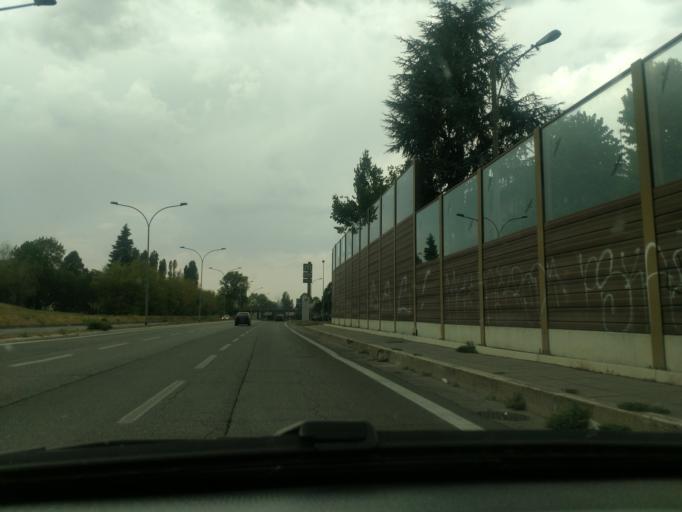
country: IT
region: Emilia-Romagna
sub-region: Provincia di Bologna
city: Casalecchio di Reno
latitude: 44.5075
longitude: 11.2826
